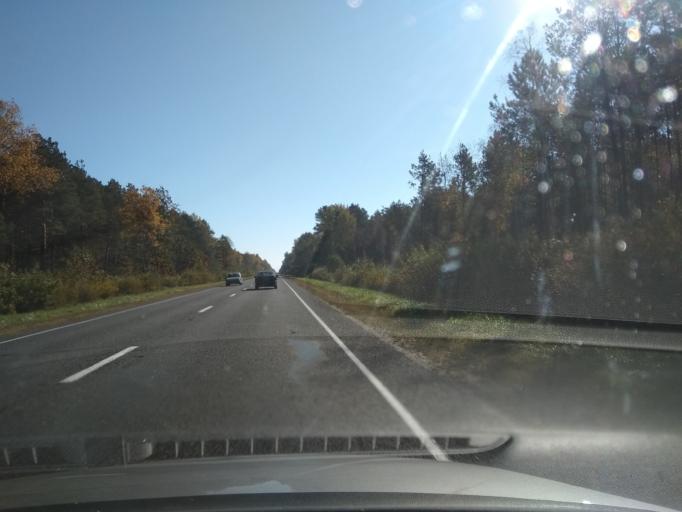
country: BY
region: Brest
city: Malaryta
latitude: 51.8998
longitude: 24.1244
